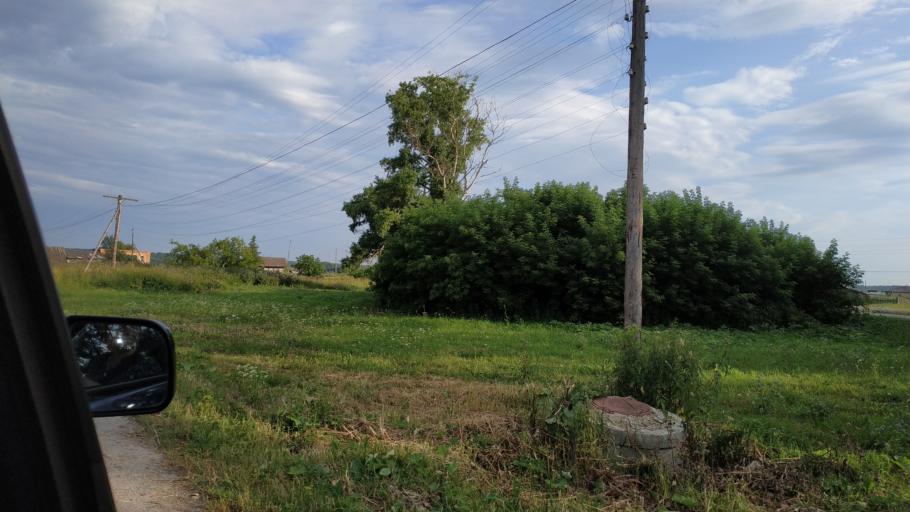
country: RU
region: Sverdlovsk
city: Yelanskiy
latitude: 57.0846
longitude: 62.4756
